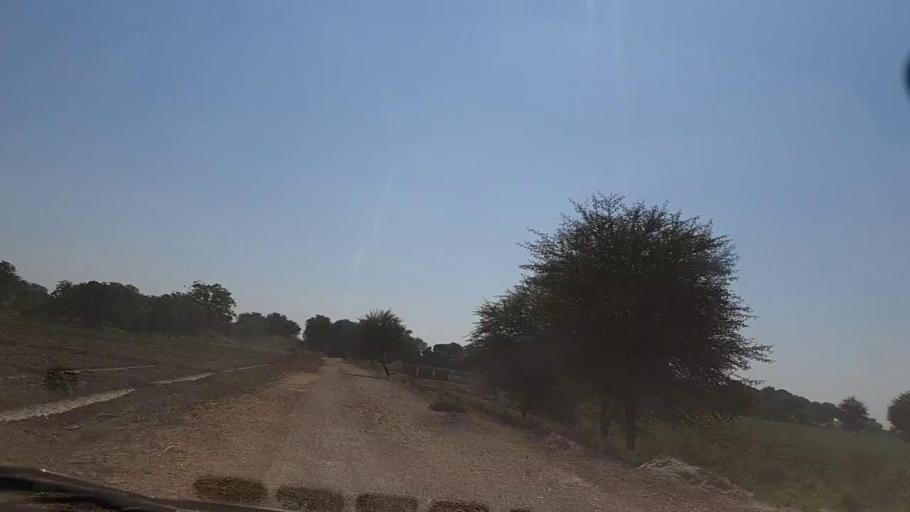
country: PK
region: Sindh
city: Mirpur Khas
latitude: 25.4278
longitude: 69.0559
